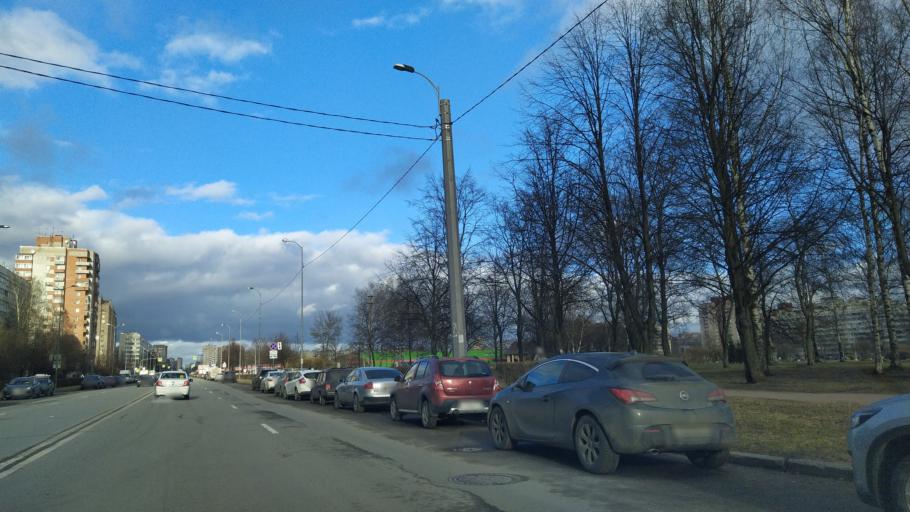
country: RU
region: St.-Petersburg
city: Grazhdanka
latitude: 60.0391
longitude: 30.3837
